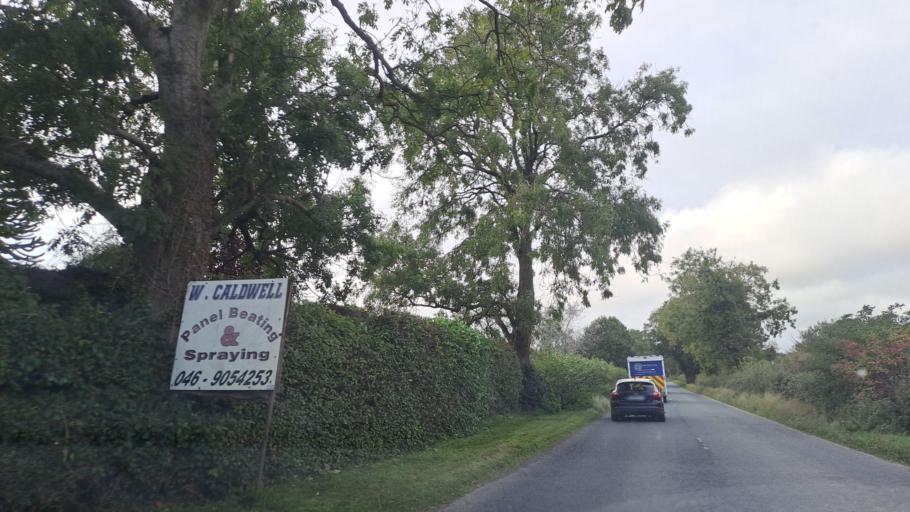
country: IE
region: Leinster
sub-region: An Mhi
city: Navan
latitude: 53.7145
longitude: -6.6940
